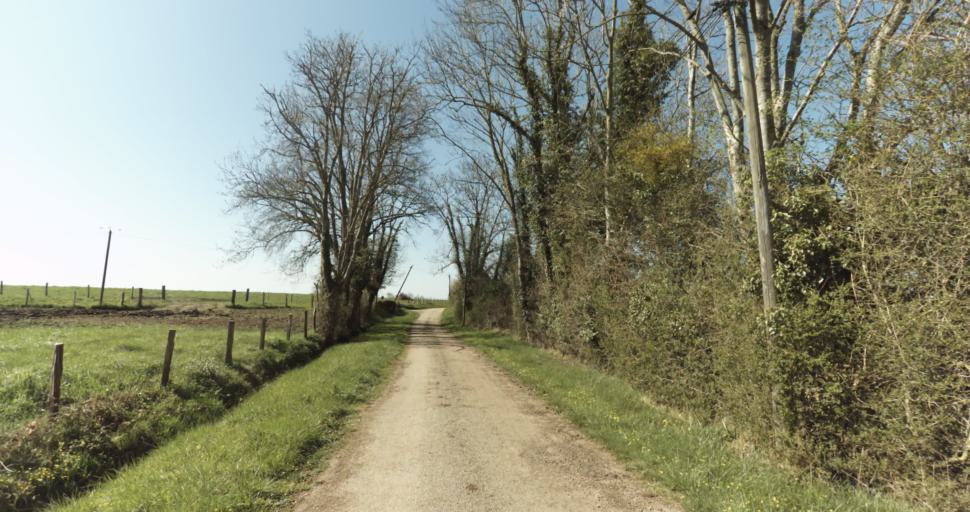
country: FR
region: Lower Normandy
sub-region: Departement du Calvados
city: Saint-Pierre-sur-Dives
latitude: 49.0036
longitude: 0.0377
